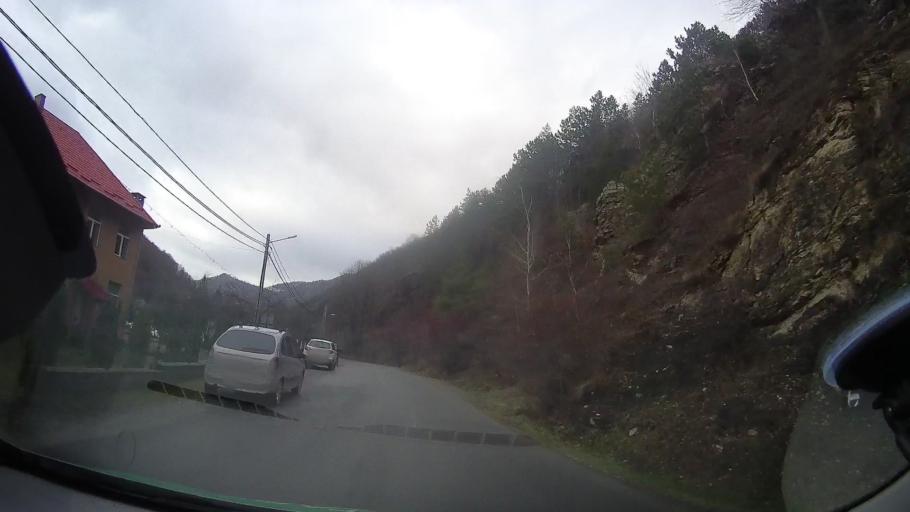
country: RO
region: Cluj
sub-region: Comuna Valea Ierii
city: Valea Ierii
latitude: 46.6476
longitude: 23.3399
